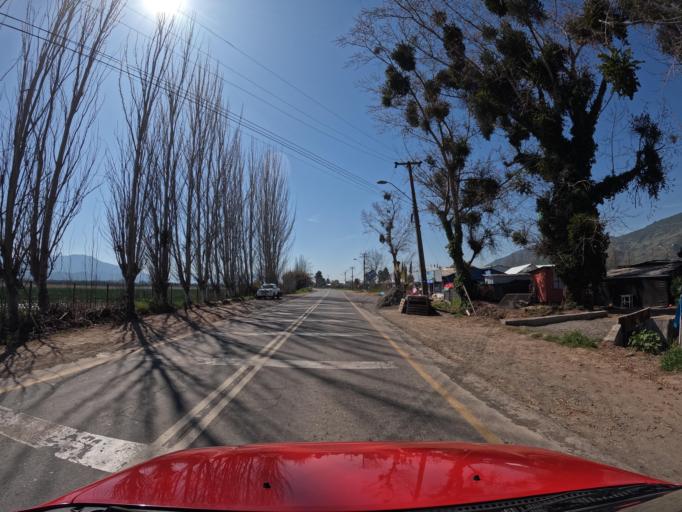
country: CL
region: Maule
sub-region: Provincia de Curico
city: Rauco
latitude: -35.0216
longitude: -71.4299
